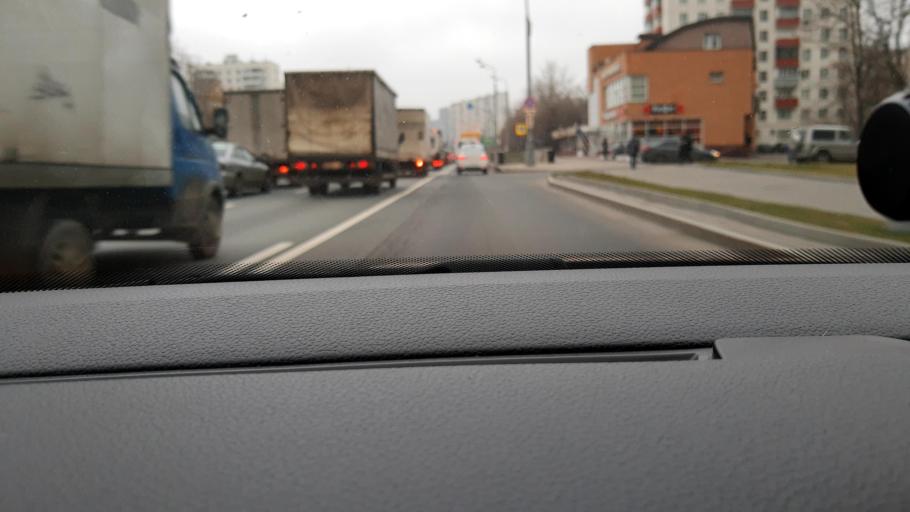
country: RU
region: Moscow
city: Metrogorodok
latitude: 55.8108
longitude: 37.7897
